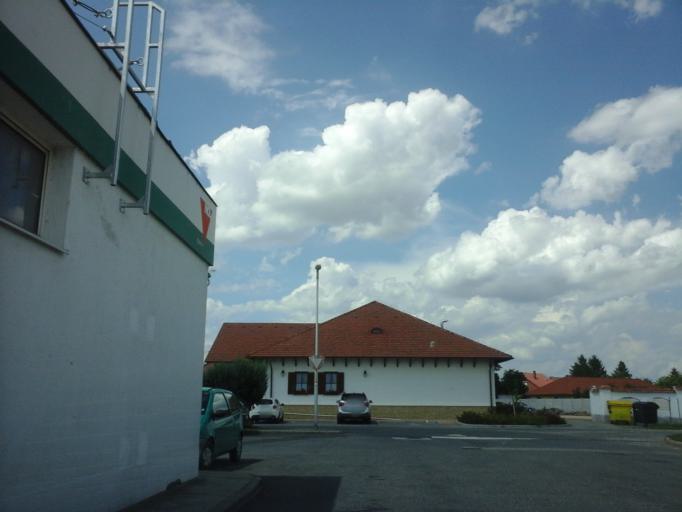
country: HU
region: Gyor-Moson-Sopron
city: Rajka
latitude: 47.9912
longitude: 17.1962
